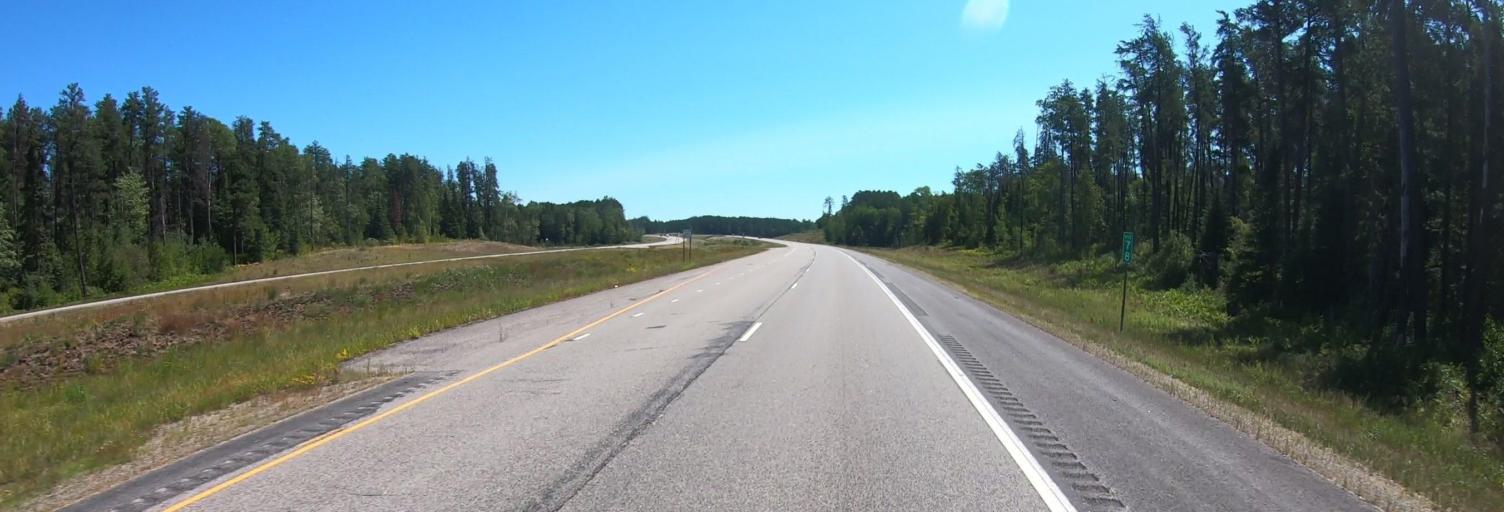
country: US
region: Minnesota
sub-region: Saint Louis County
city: Mountain Iron
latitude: 47.6600
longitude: -92.6182
